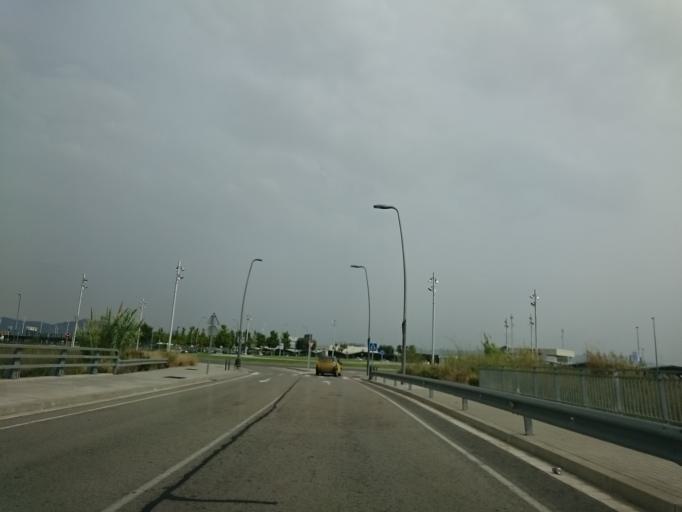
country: ES
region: Catalonia
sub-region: Provincia de Barcelona
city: Viladecans
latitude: 41.2904
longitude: 2.0553
